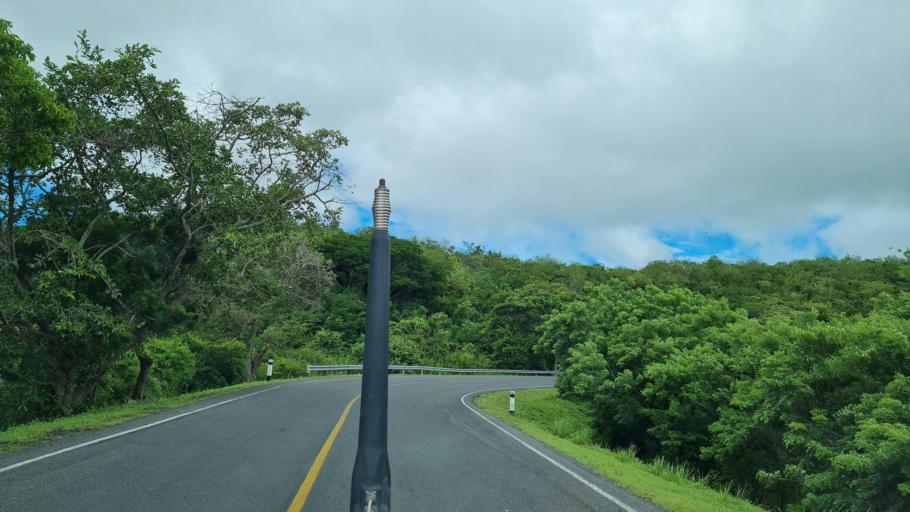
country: NI
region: Matagalpa
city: Terrabona
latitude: 12.5830
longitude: -85.9795
